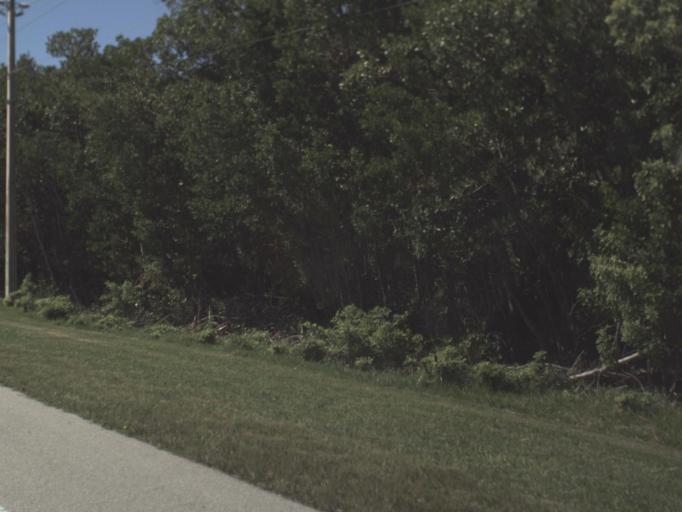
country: US
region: Florida
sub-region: Collier County
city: Marco
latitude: 25.9754
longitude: -81.7057
